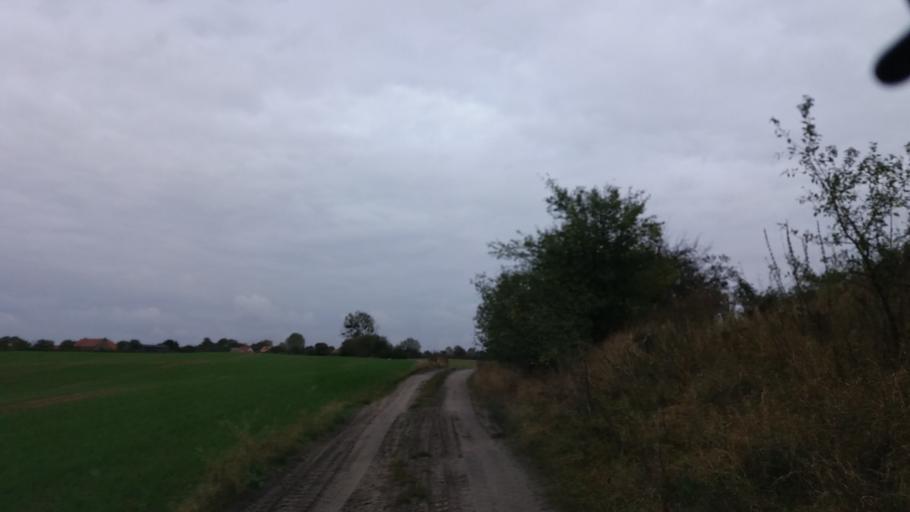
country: PL
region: West Pomeranian Voivodeship
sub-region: Powiat choszczenski
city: Pelczyce
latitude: 53.0321
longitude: 15.3243
